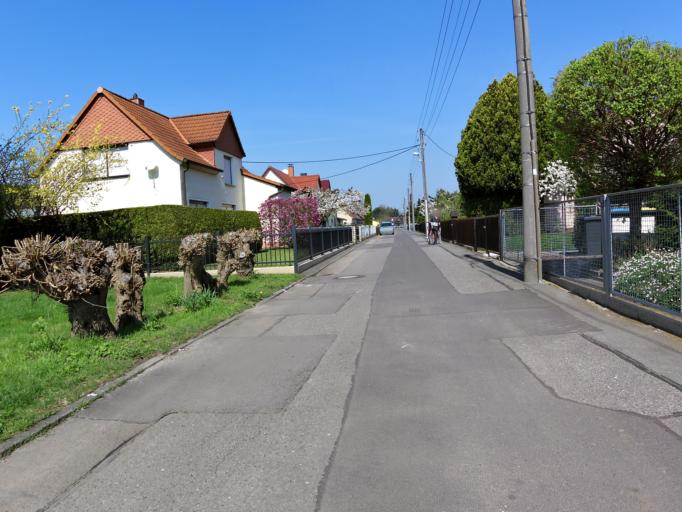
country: DE
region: Saxony
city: Leipzig
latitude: 51.3842
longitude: 12.3264
